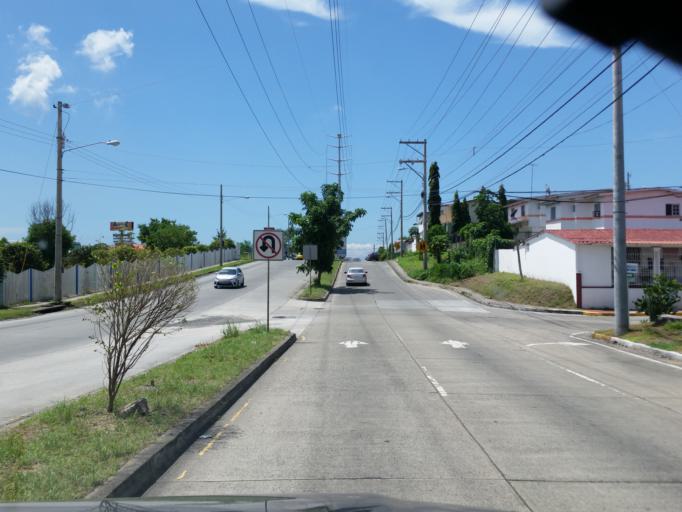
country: PA
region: Panama
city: San Miguelito
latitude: 9.0547
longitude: -79.4614
